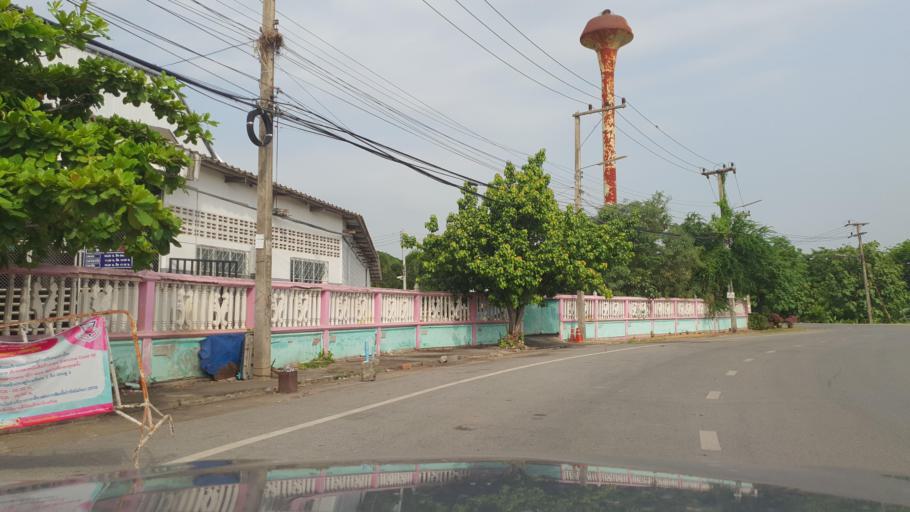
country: TH
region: Phitsanulok
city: Phitsanulok
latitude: 16.8422
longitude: 100.2628
